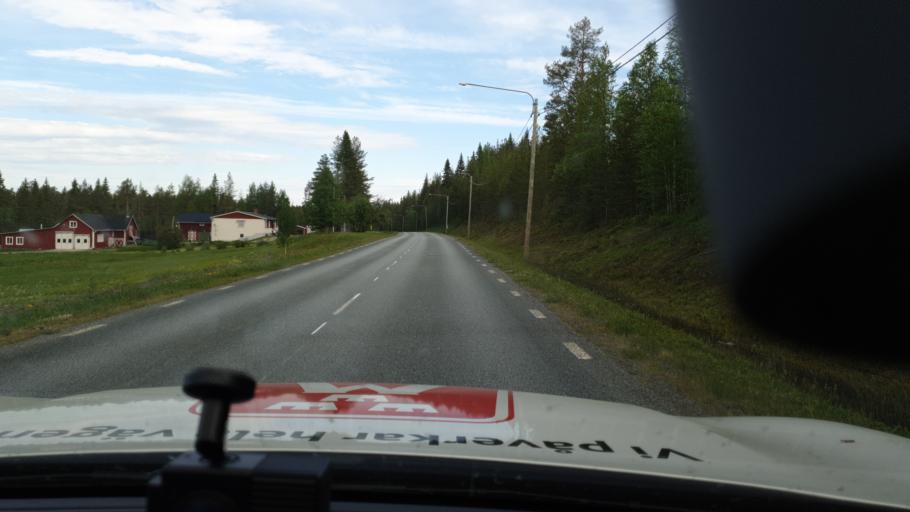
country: SE
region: Vaesterbotten
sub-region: Lycksele Kommun
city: Soderfors
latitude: 65.1163
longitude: 18.2947
